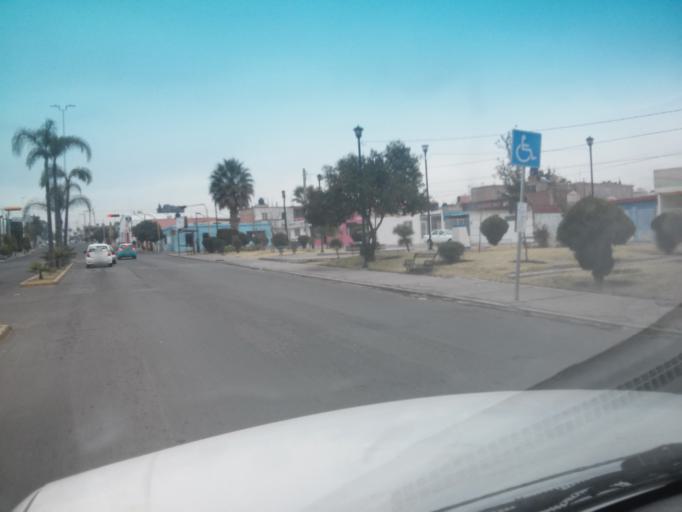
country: MX
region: Durango
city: Victoria de Durango
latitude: 24.0116
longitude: -104.6780
